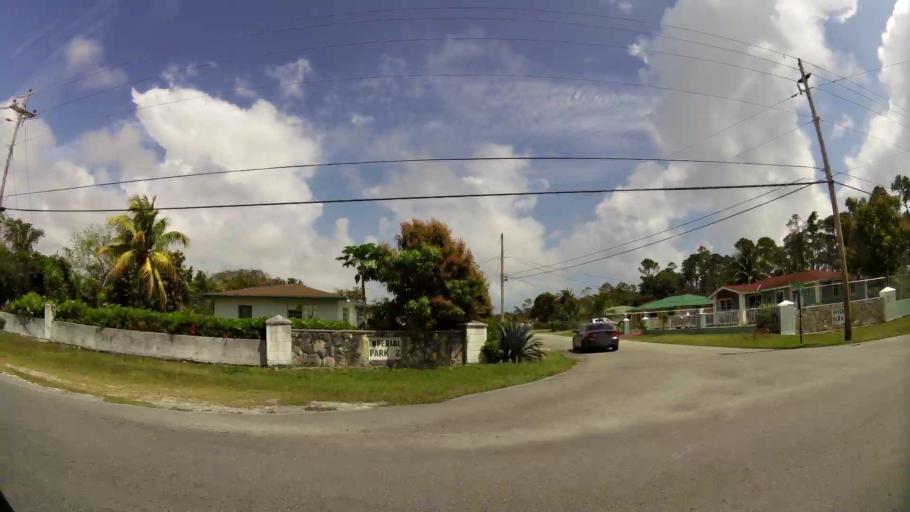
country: BS
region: Freeport
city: Freeport
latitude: 26.5087
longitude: -78.6912
